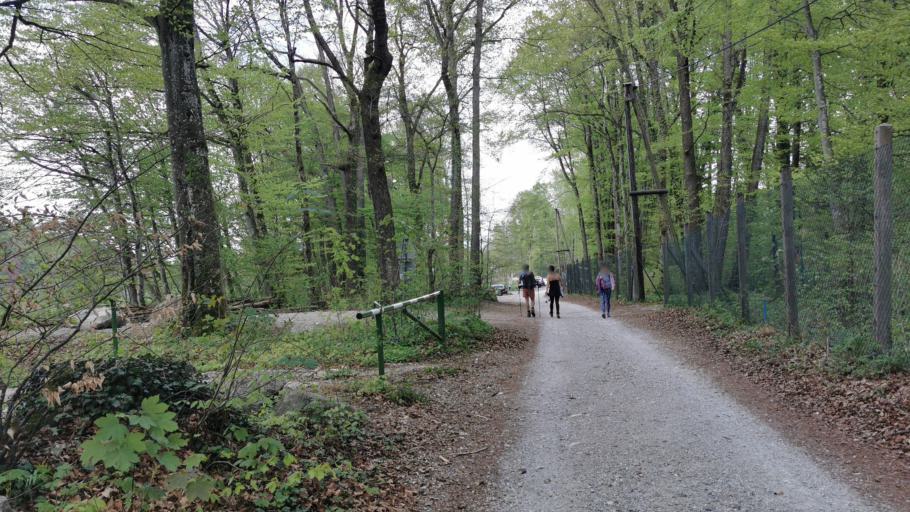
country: AT
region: Salzburg
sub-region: Politischer Bezirk Salzburg-Umgebung
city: Grodig
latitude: 47.7459
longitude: 13.0122
